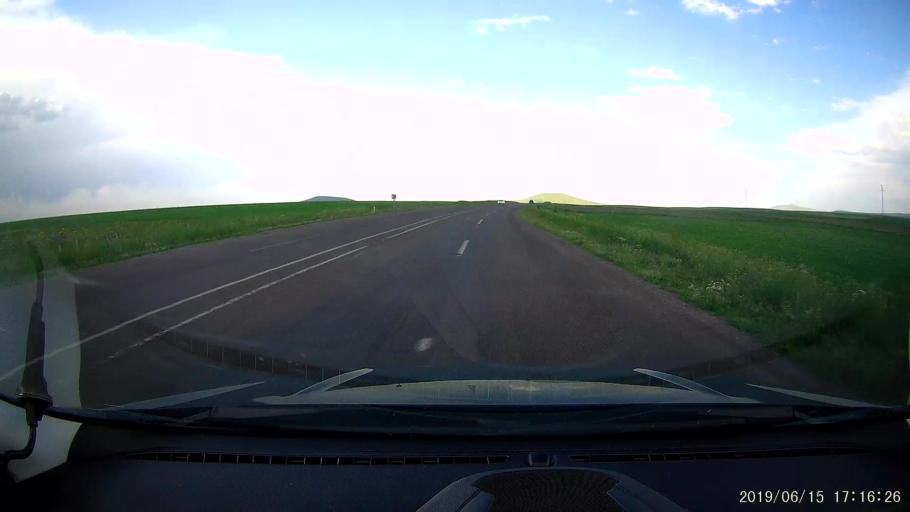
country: TR
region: Kars
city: Kars
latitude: 40.6147
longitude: 43.2176
